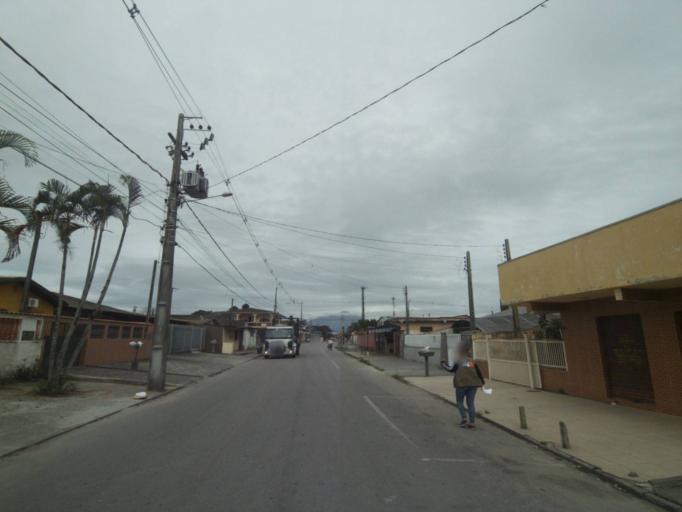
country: BR
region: Parana
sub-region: Paranagua
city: Paranagua
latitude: -25.5164
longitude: -48.5319
